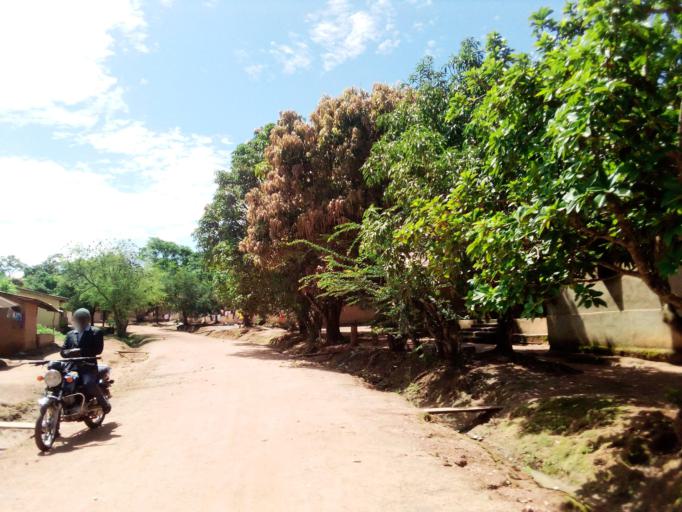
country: SL
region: Eastern Province
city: Koidu
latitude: 8.6667
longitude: -10.9453
